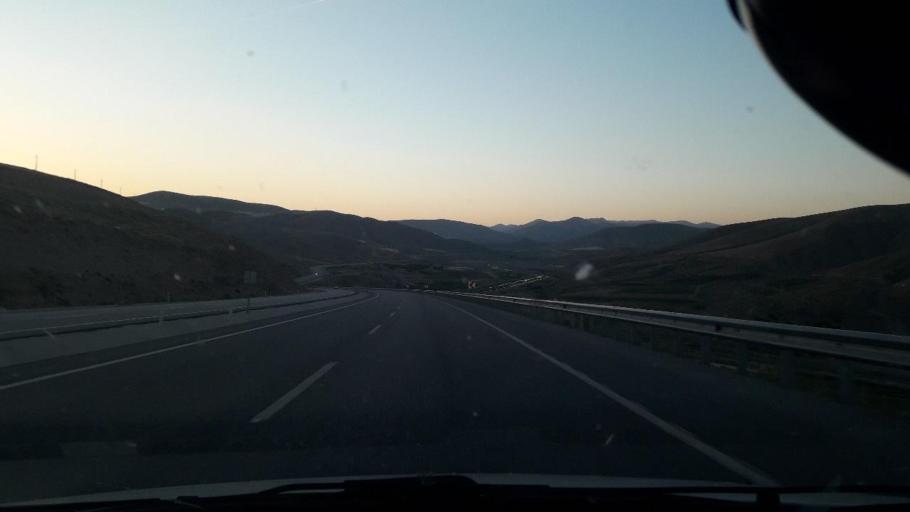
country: TR
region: Malatya
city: Yazihan
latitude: 38.6179
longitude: 38.1708
